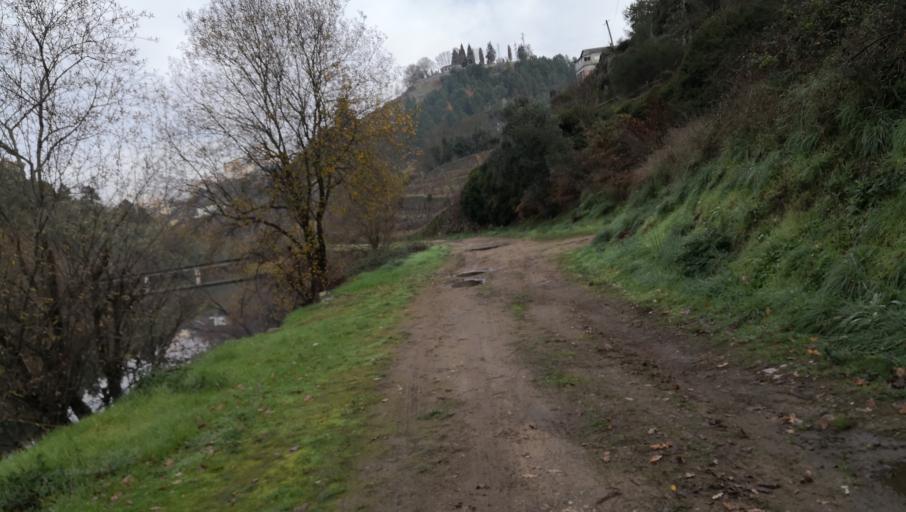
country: PT
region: Vila Real
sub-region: Vila Real
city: Vila Real
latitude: 41.2865
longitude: -7.7491
